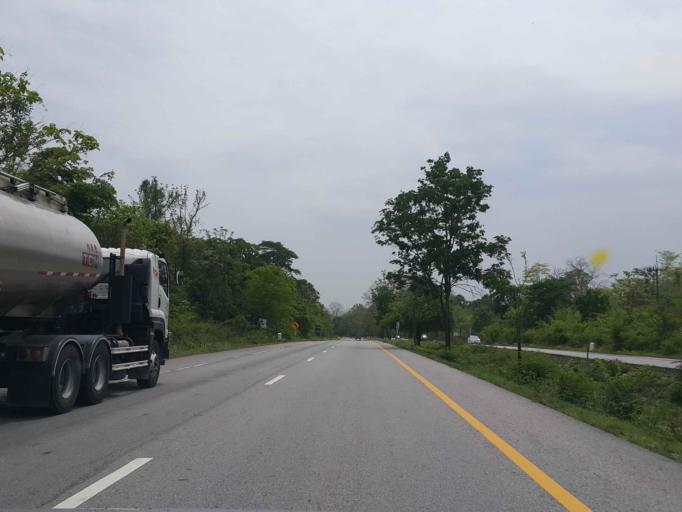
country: TH
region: Lampang
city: Sop Prap
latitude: 17.8103
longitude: 99.2691
